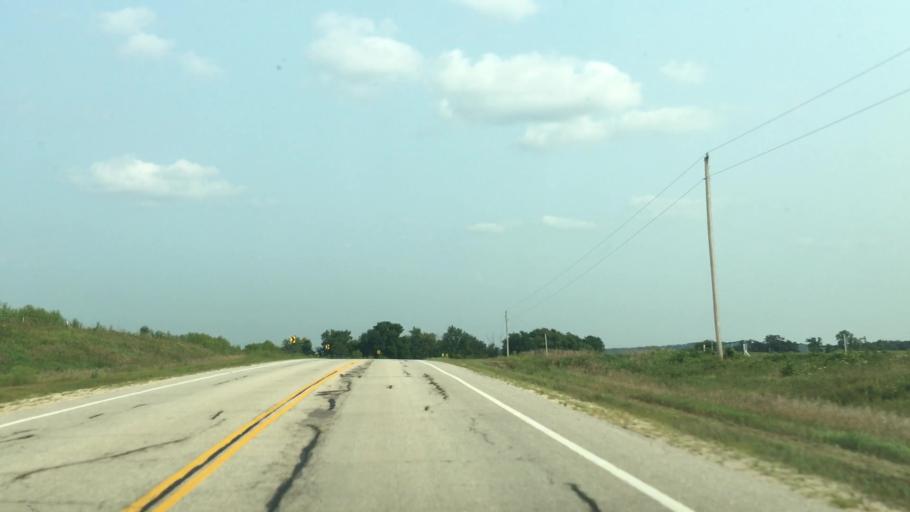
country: US
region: Minnesota
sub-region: Fillmore County
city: Preston
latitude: 43.6897
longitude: -91.9455
